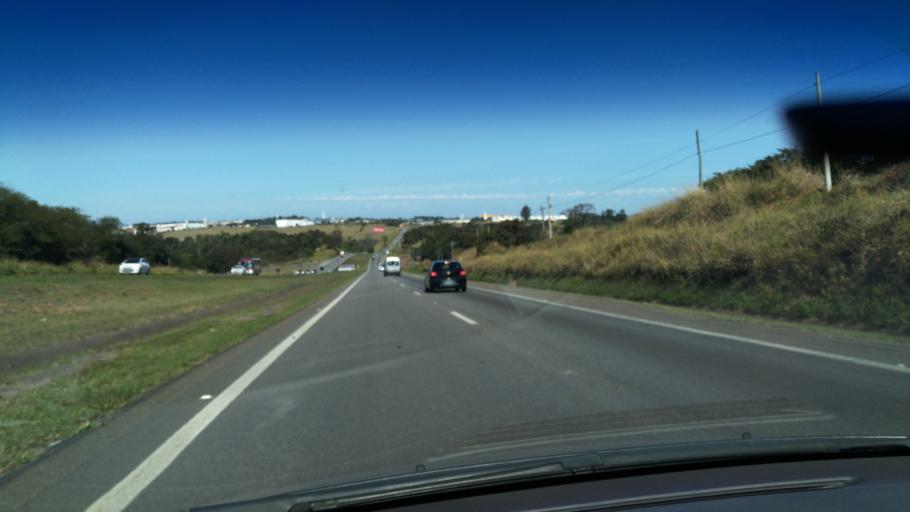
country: BR
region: Sao Paulo
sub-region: Jaguariuna
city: Jaguariuna
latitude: -22.6536
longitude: -47.0047
